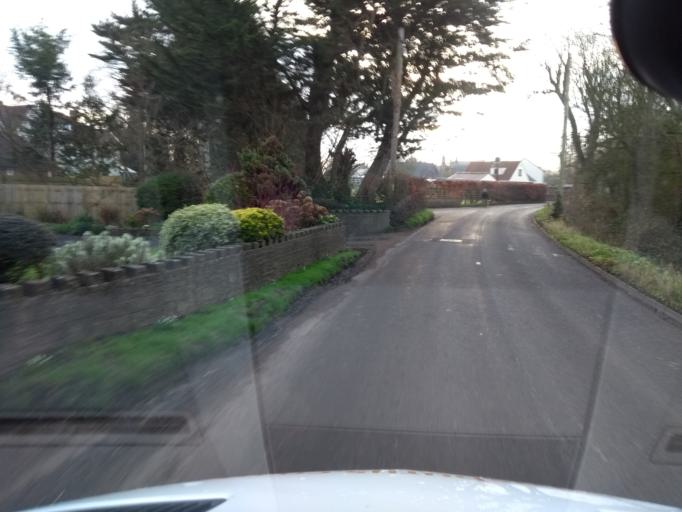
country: GB
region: England
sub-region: North Somerset
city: Bleadon
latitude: 51.2858
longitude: -2.9559
